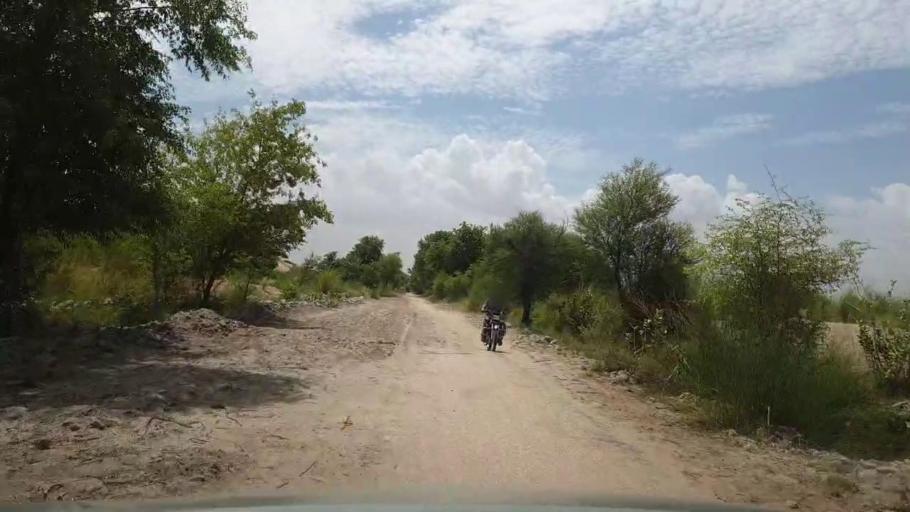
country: PK
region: Sindh
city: Bozdar
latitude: 27.0638
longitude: 68.9629
